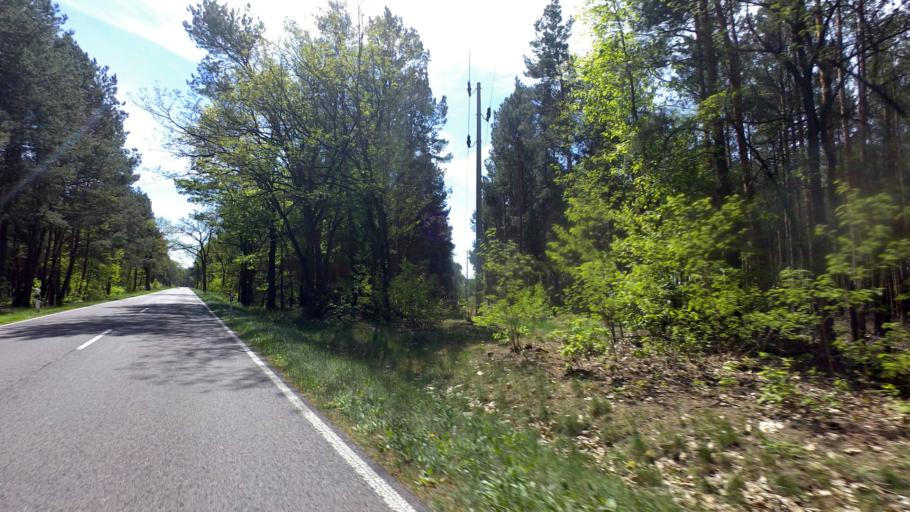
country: DE
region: Brandenburg
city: Luckenwalde
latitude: 52.1476
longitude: 13.1125
